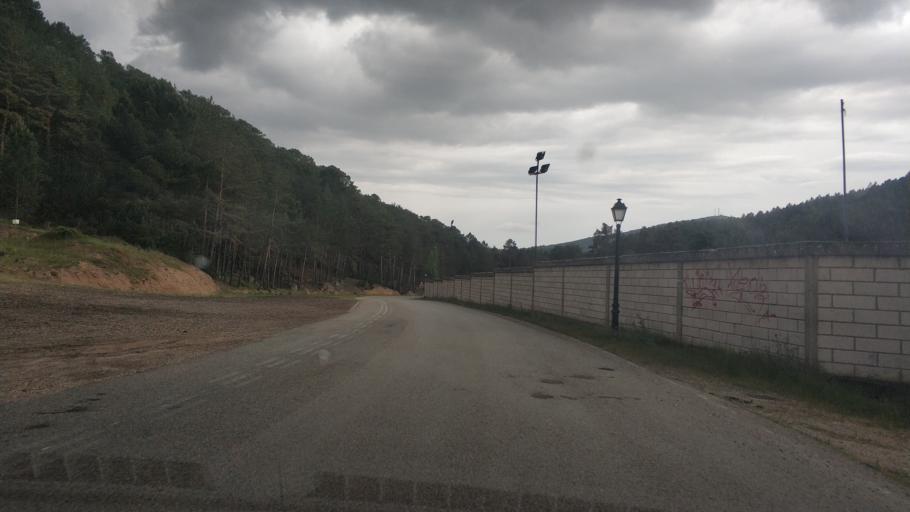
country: ES
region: Castille and Leon
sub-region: Provincia de Soria
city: San Leonardo de Yague
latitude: 41.8395
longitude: -3.0652
